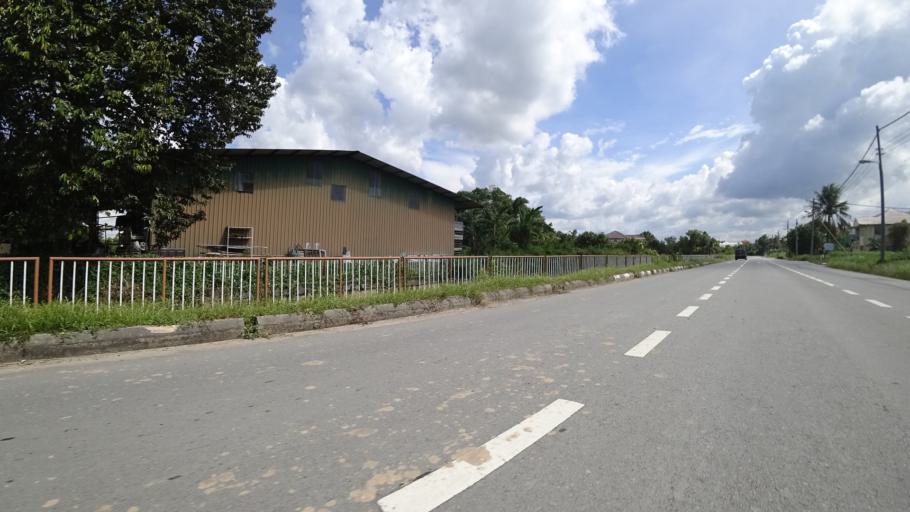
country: BN
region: Brunei and Muara
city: Bandar Seri Begawan
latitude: 4.8735
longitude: 114.8600
